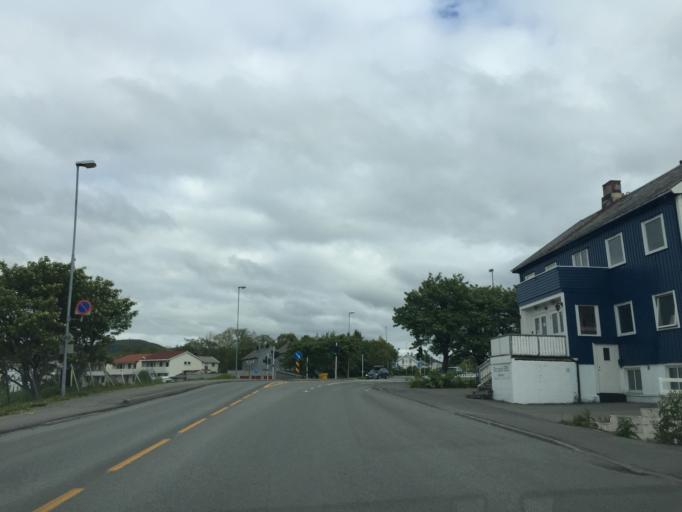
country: NO
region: Nordland
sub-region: Bodo
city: Bodo
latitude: 67.2862
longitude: 14.3973
